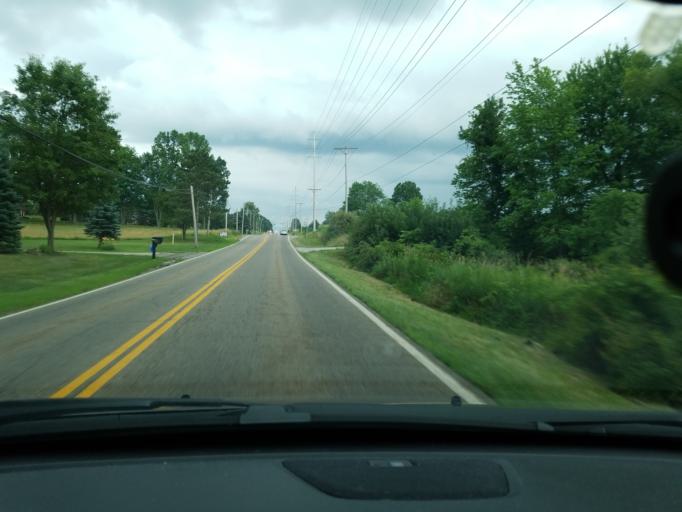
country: US
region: Ohio
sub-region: Summit County
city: Greensburg
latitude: 40.8974
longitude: -81.4984
